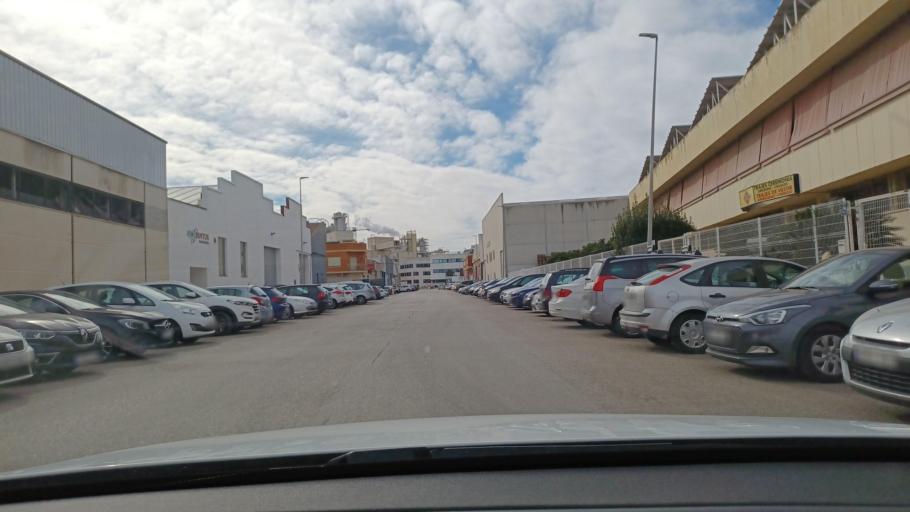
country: ES
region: Valencia
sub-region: Provincia de Valencia
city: Benifaio
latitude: 39.2865
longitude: -0.4321
